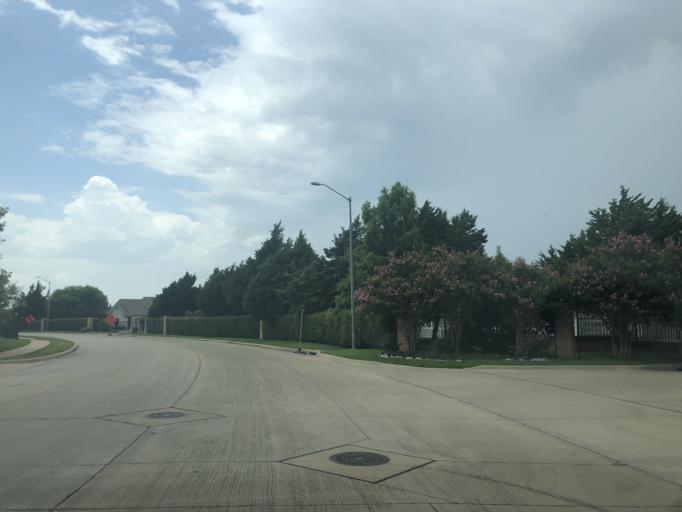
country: US
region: Texas
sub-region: Dallas County
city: Grand Prairie
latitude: 32.7343
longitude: -97.0169
